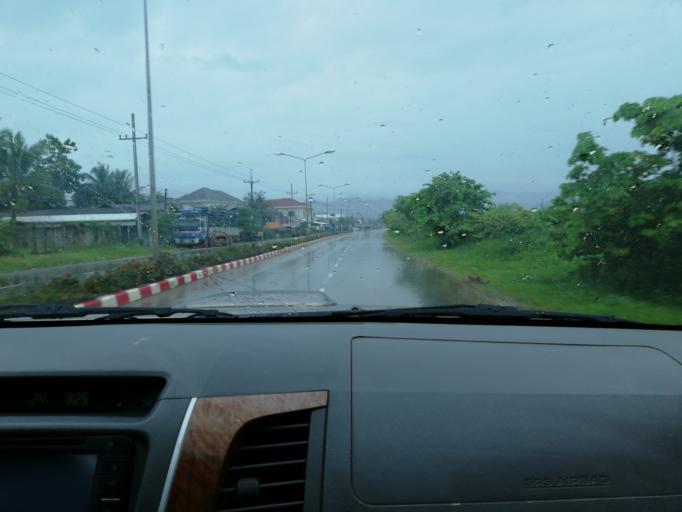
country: LA
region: Loungnamtha
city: Louang Namtha
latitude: 20.9550
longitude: 101.4038
